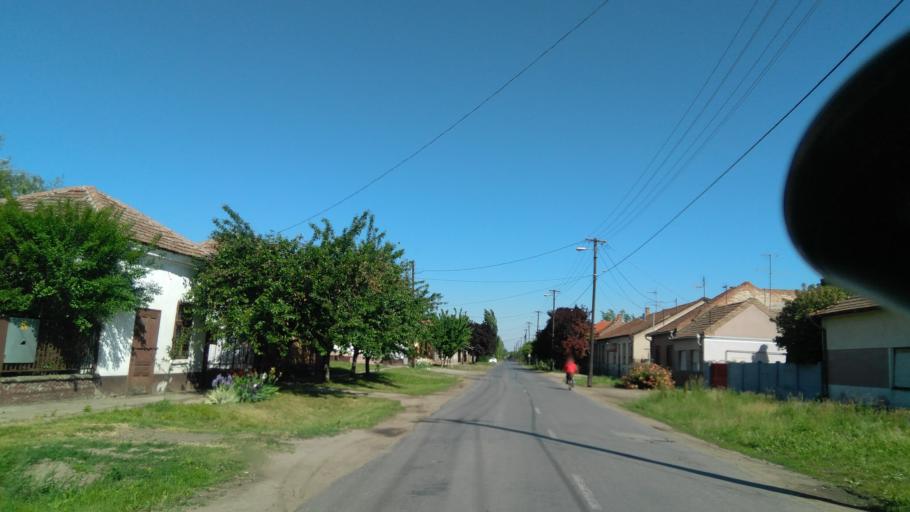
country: HU
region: Bekes
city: Kevermes
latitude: 46.4164
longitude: 21.1805
